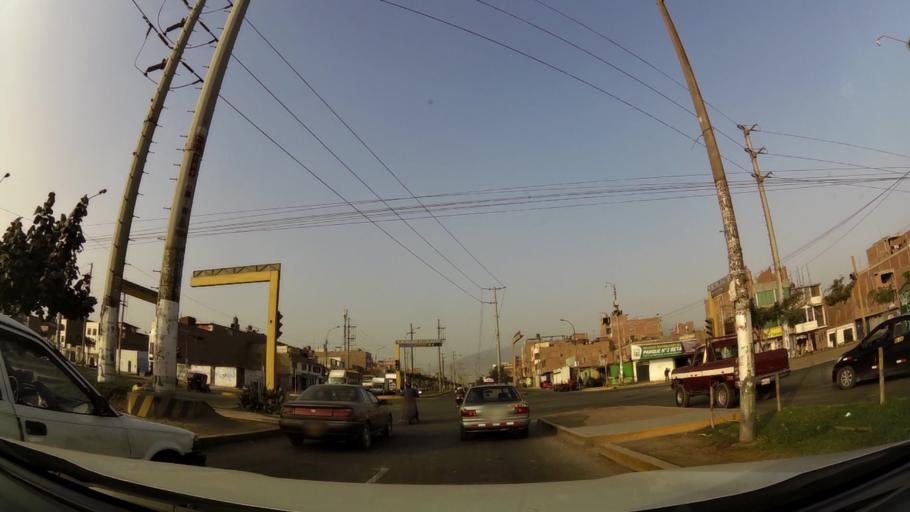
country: PE
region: Lima
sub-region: Lima
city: Independencia
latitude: -11.9478
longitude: -77.0773
